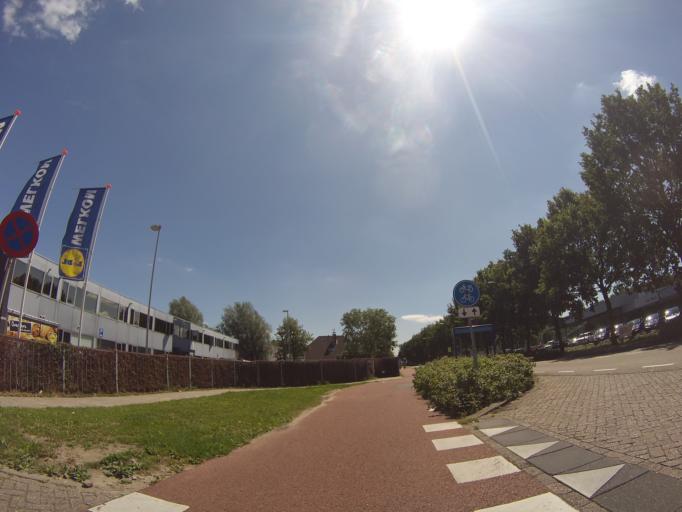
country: NL
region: Utrecht
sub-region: Stichtse Vecht
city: Maarssen
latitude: 52.1290
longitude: 5.0372
